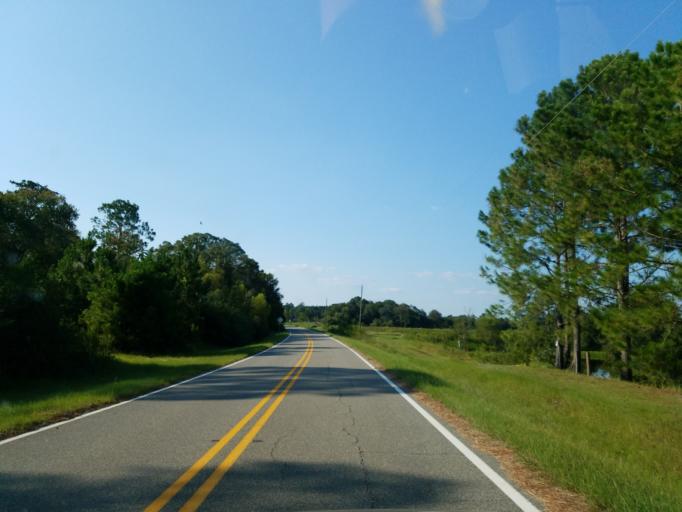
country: US
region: Georgia
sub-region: Lowndes County
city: Hahira
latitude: 31.0222
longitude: -83.3888
